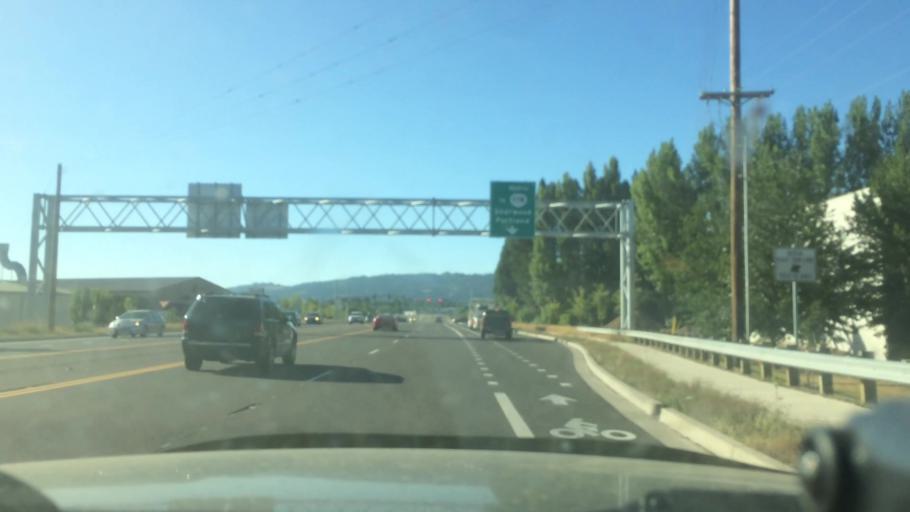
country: US
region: Oregon
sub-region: Yamhill County
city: Newberg
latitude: 45.2917
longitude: -122.9483
